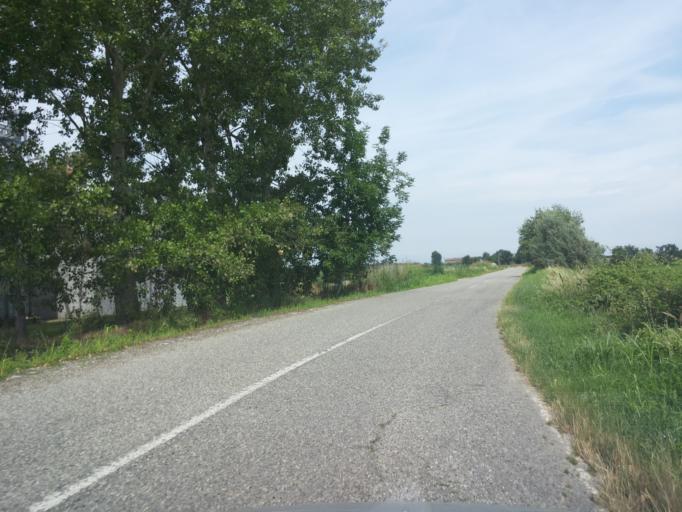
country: IT
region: Piedmont
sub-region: Provincia di Vercelli
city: Caresana
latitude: 45.2259
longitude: 8.4995
